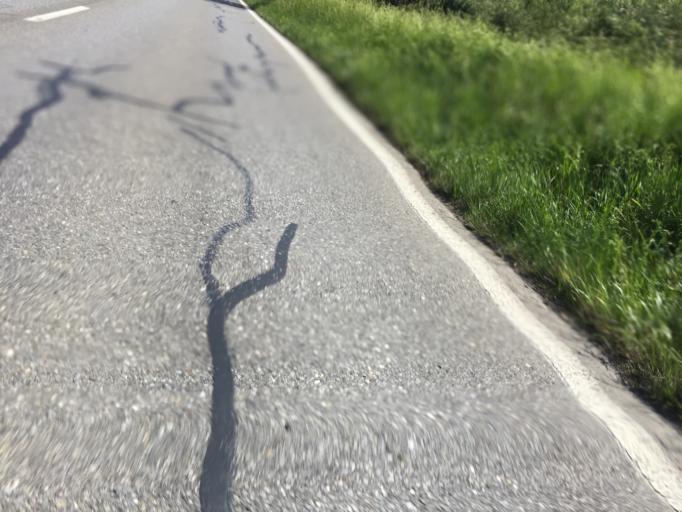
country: CH
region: Bern
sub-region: Bern-Mittelland District
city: Konolfingen
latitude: 46.8854
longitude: 7.6341
